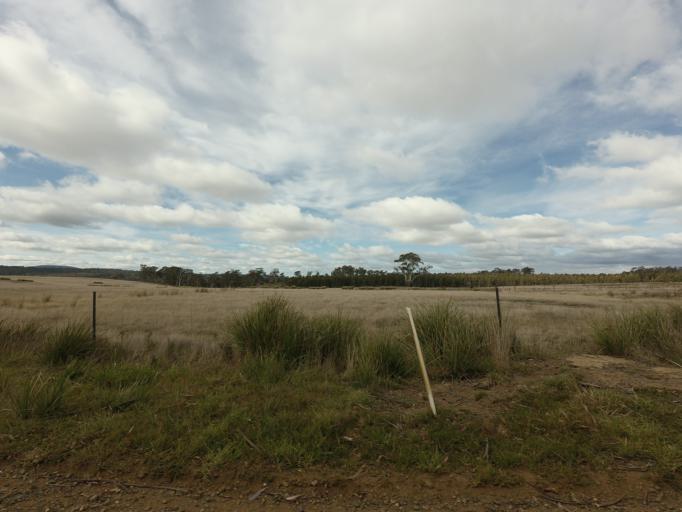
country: AU
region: Tasmania
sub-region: Brighton
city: Bridgewater
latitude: -42.4384
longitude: 147.3857
